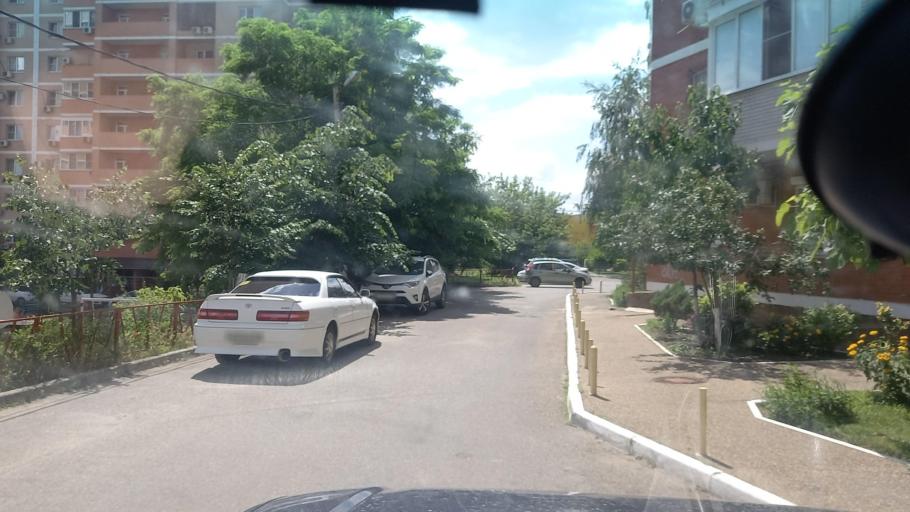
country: RU
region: Krasnodarskiy
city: Krasnodar
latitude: 45.0373
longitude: 38.9355
